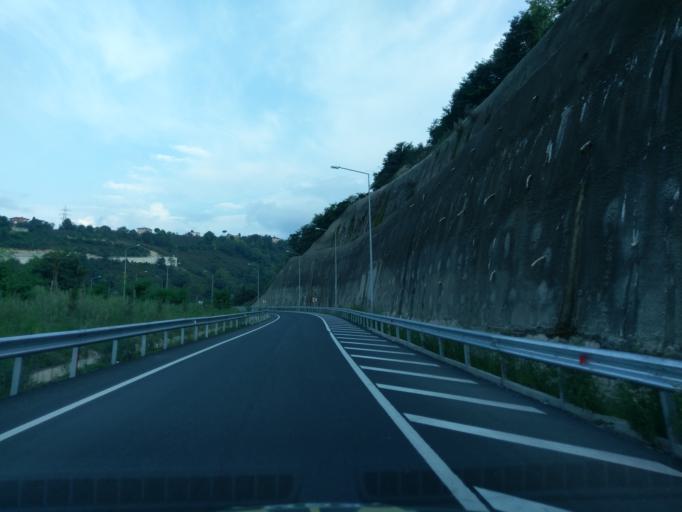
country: TR
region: Ordu
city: Ordu
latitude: 40.9885
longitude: 37.8090
